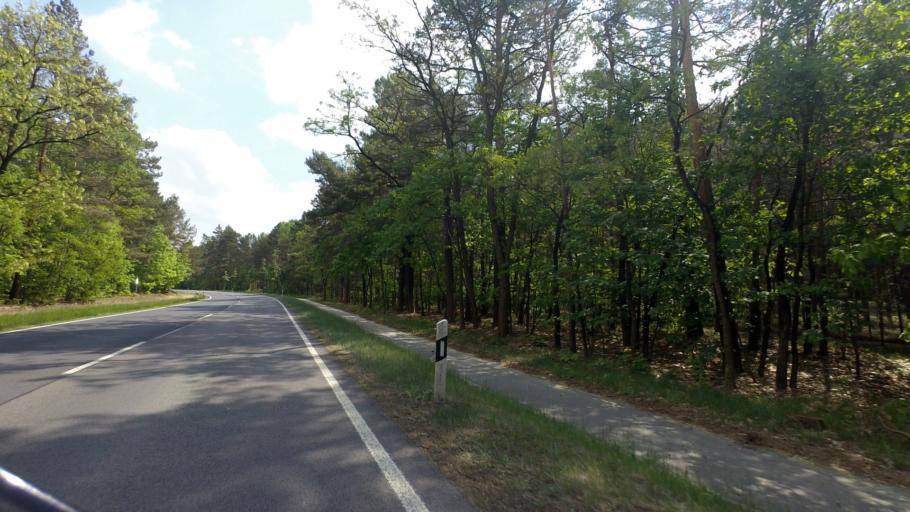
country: DE
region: Saxony
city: Weisskeissel
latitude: 51.4703
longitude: 14.7296
